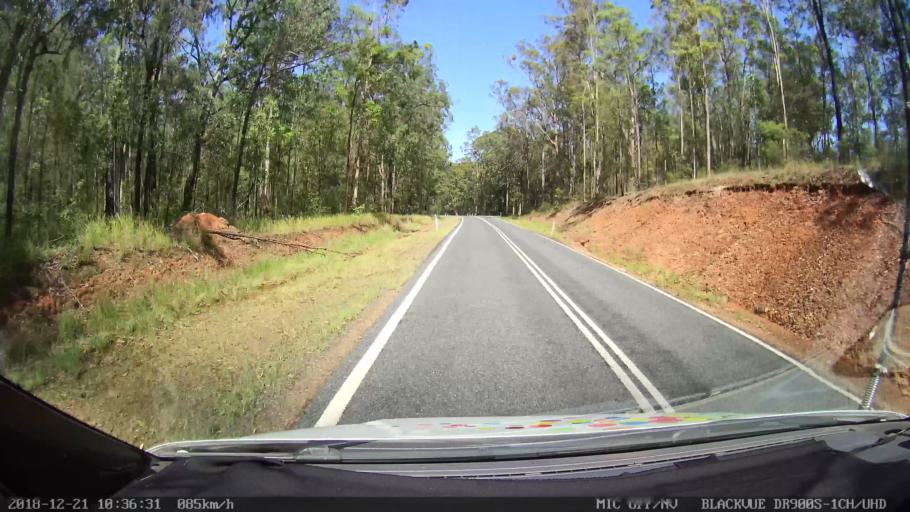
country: AU
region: New South Wales
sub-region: Clarence Valley
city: South Grafton
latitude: -29.6222
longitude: 152.6316
